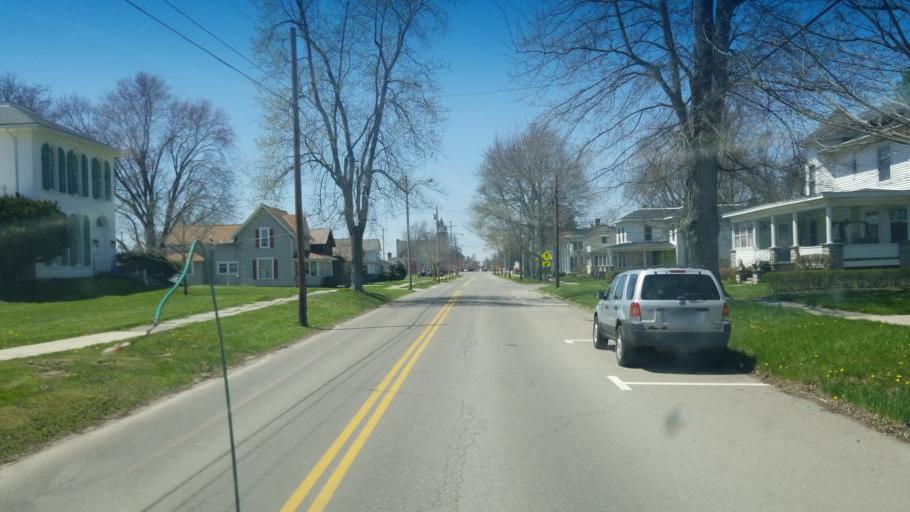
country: US
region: Ohio
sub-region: Huron County
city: New London
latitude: 41.0849
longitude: -82.3940
